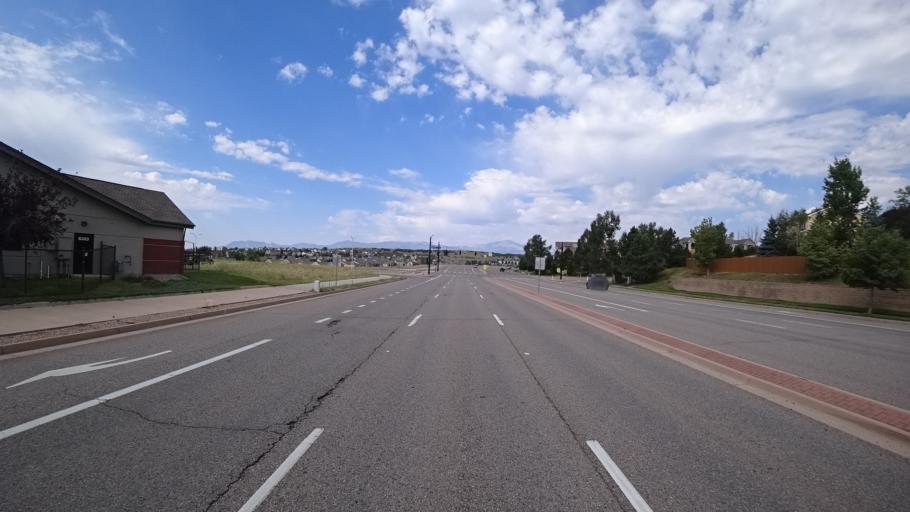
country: US
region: Colorado
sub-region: El Paso County
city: Cimarron Hills
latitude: 38.9101
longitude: -104.7096
